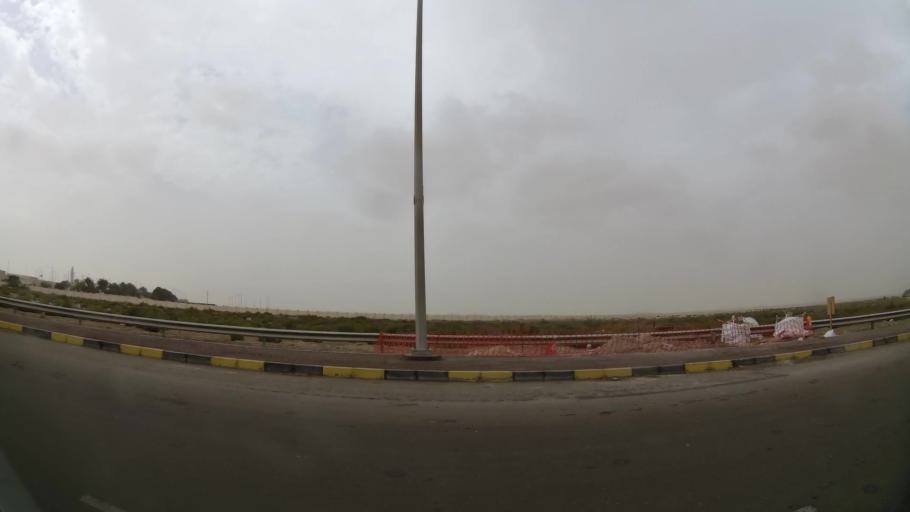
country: AE
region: Abu Dhabi
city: Abu Dhabi
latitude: 24.3809
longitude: 54.6872
